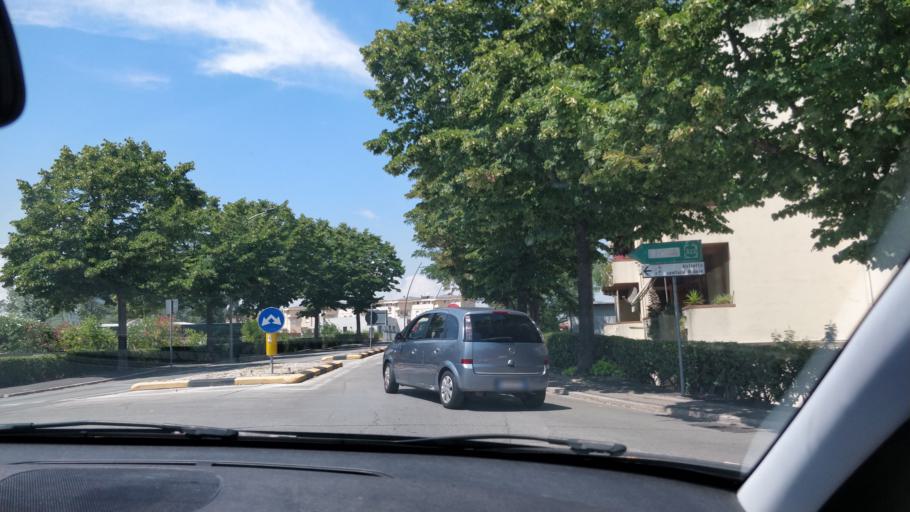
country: IT
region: Abruzzo
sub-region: Provincia di Chieti
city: Francavilla al Mare
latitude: 42.4237
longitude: 14.2801
